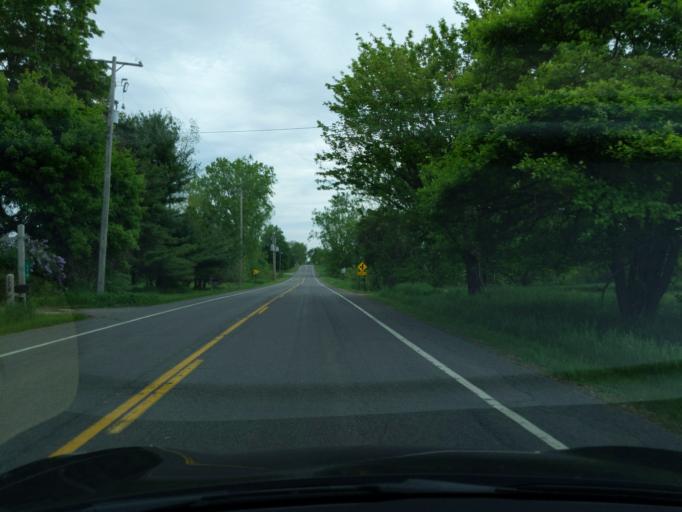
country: US
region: Michigan
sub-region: Ingham County
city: Mason
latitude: 42.5797
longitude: -84.3572
